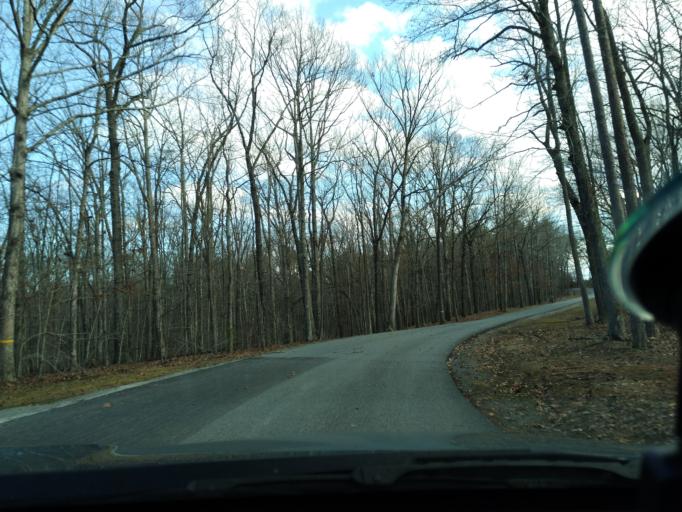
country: US
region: Virginia
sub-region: Nottoway County
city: Crewe
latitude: 37.1785
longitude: -78.2659
